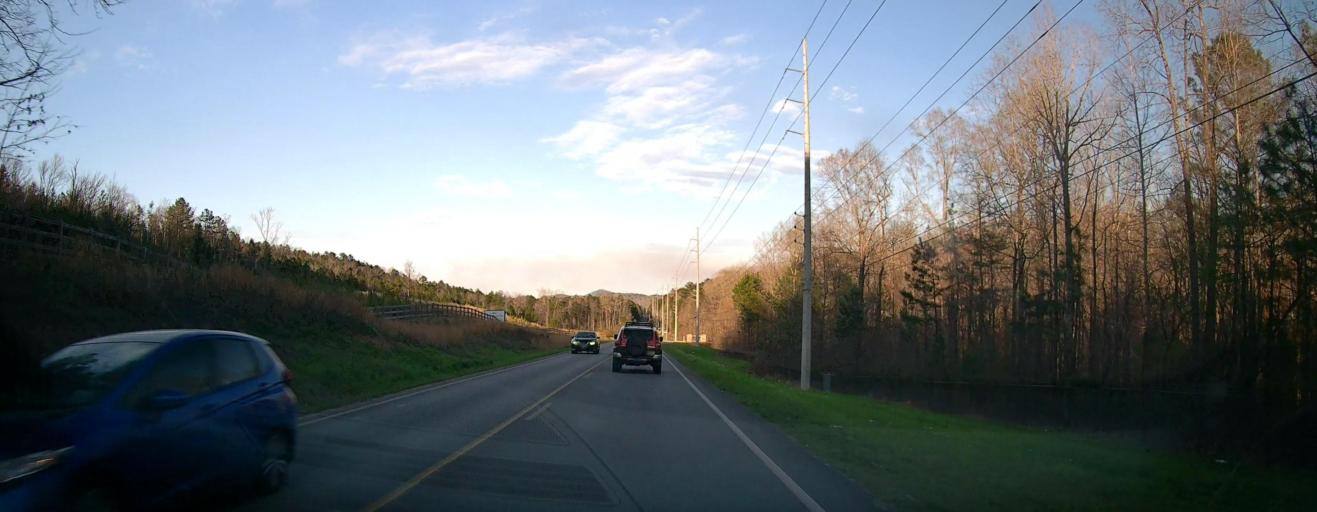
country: US
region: Alabama
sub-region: Shelby County
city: Chelsea
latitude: 33.3399
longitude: -86.6744
